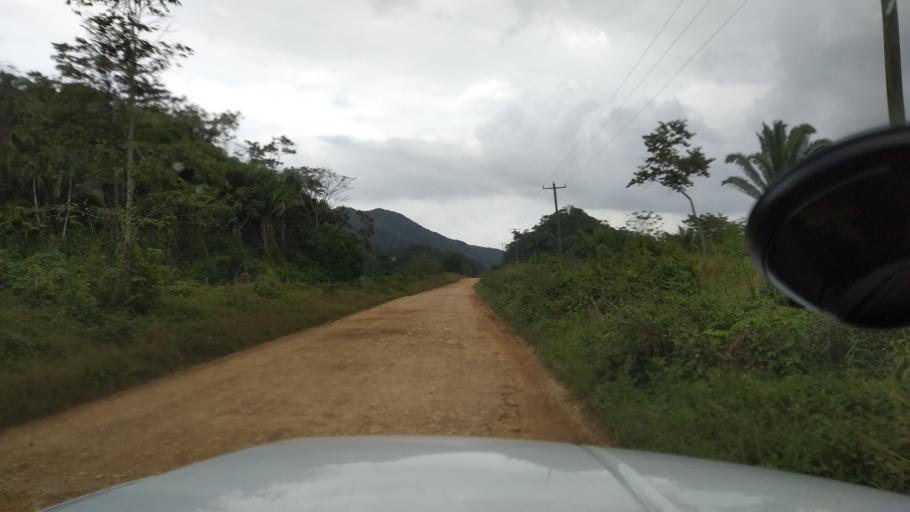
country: BZ
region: Toledo
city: Punta Gorda
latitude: 16.2035
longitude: -89.0332
